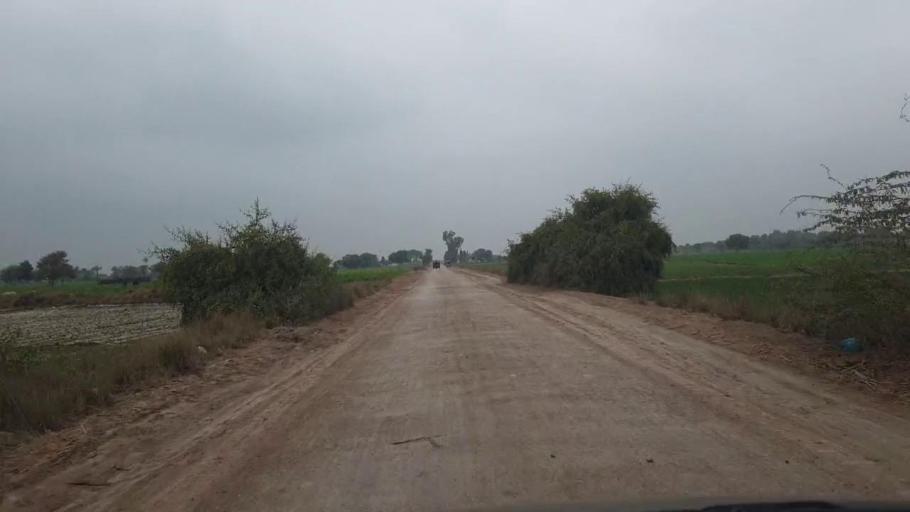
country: PK
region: Sindh
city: Shahdadpur
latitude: 25.9408
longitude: 68.7254
